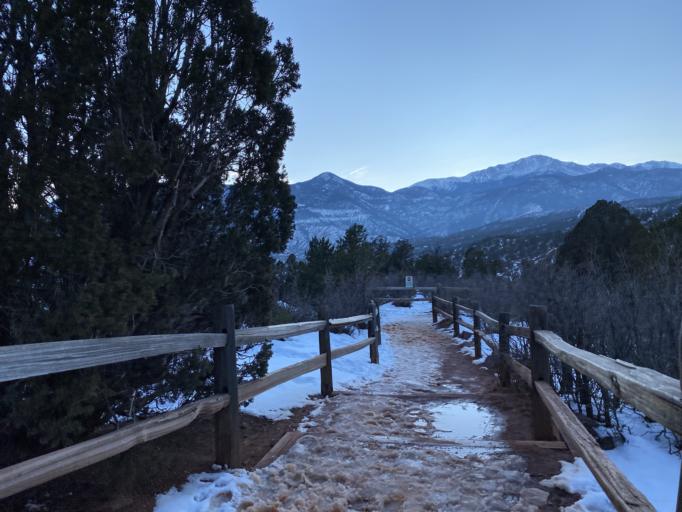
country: US
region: Colorado
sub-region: El Paso County
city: Manitou Springs
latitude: 38.8749
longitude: -104.8811
